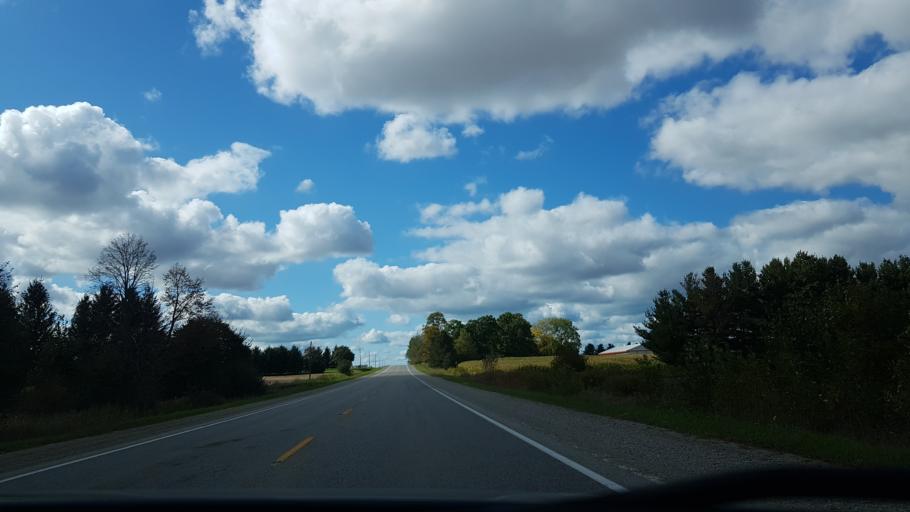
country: CA
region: Ontario
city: South Huron
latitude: 43.3527
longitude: -81.5706
